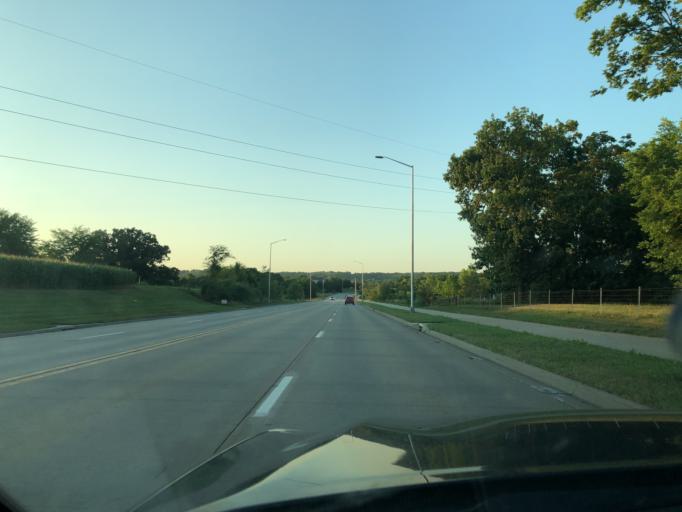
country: US
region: Kansas
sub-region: Leavenworth County
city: Leavenworth
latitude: 39.2732
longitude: -94.9468
